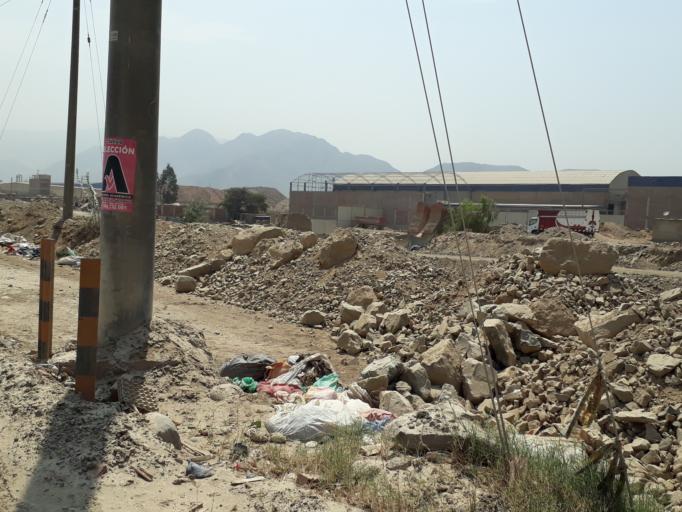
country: PE
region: Lima
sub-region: Lima
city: Santa Maria
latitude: -12.0020
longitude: -76.9181
